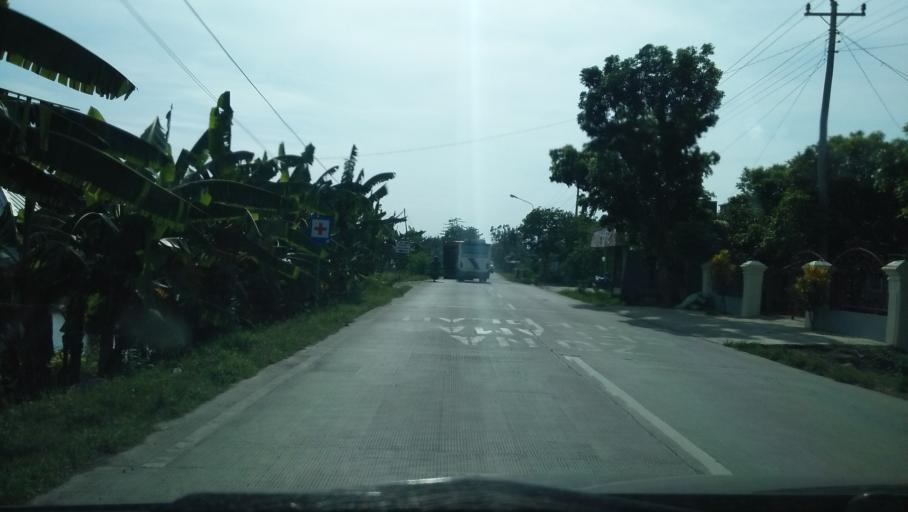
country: ID
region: Central Java
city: Welahan
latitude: -6.8544
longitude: 110.7077
